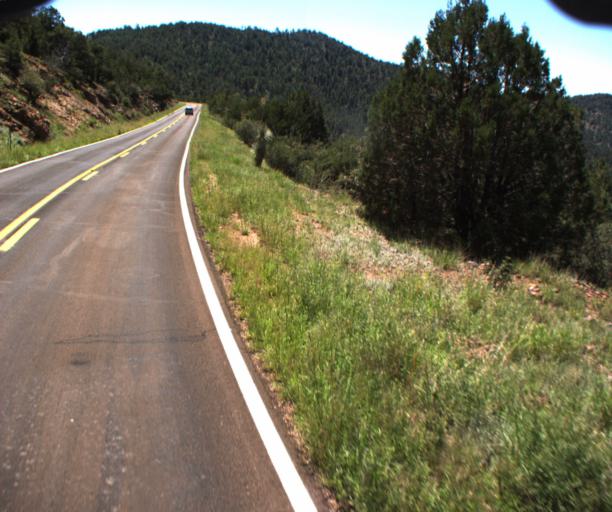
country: US
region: Arizona
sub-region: Greenlee County
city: Morenci
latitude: 33.4143
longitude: -109.3613
